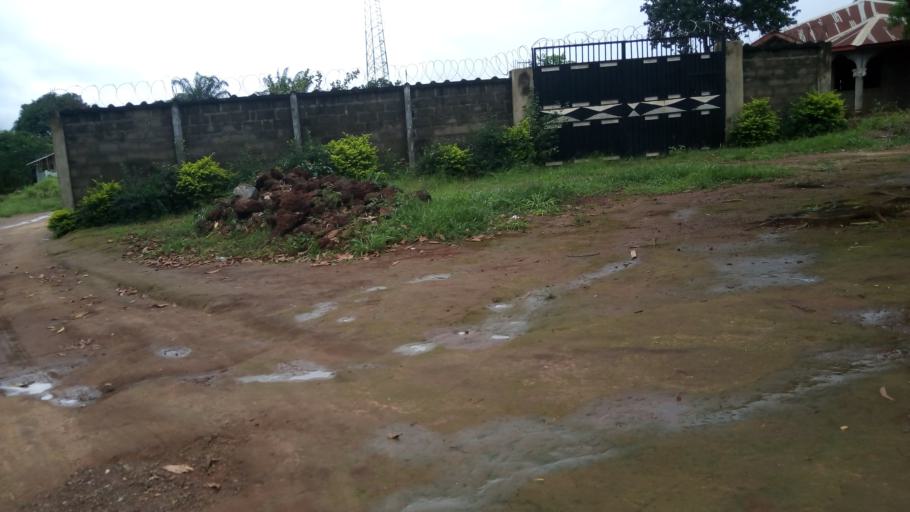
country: SL
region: Northern Province
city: Lunsar
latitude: 8.6926
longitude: -12.5315
